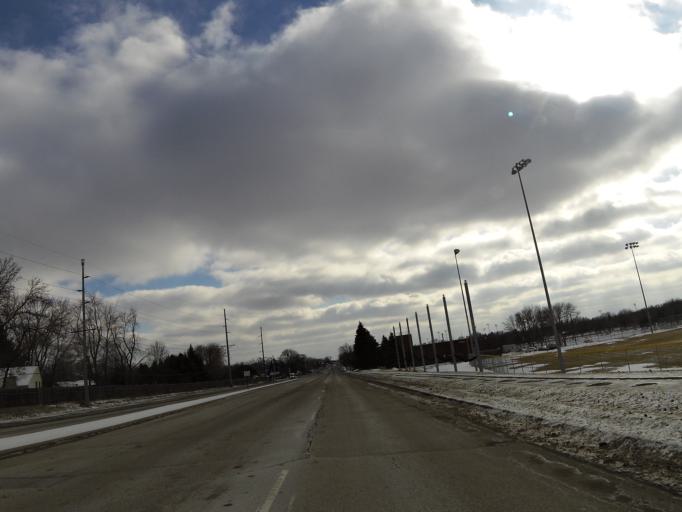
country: US
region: Minnesota
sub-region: Hennepin County
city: Eden Prairie
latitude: 44.8710
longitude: -93.4858
